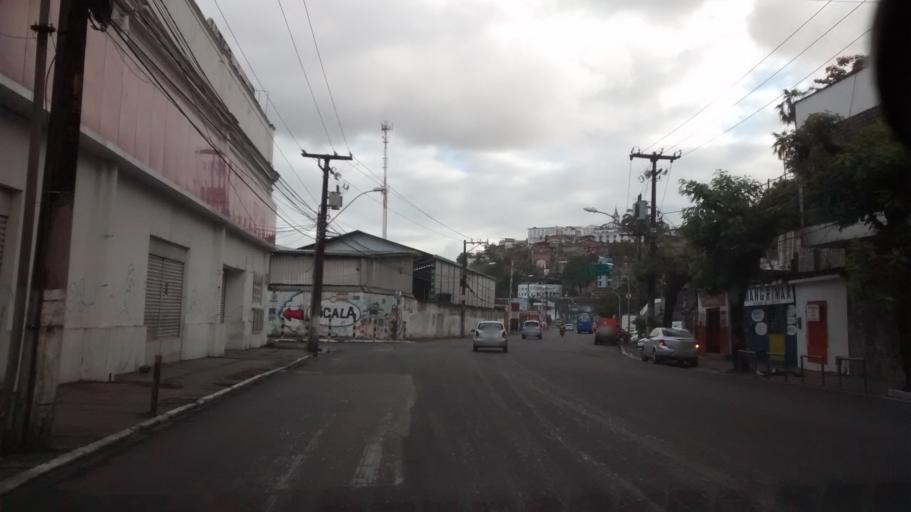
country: BR
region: Bahia
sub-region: Salvador
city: Salvador
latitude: -12.9606
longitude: -38.5038
